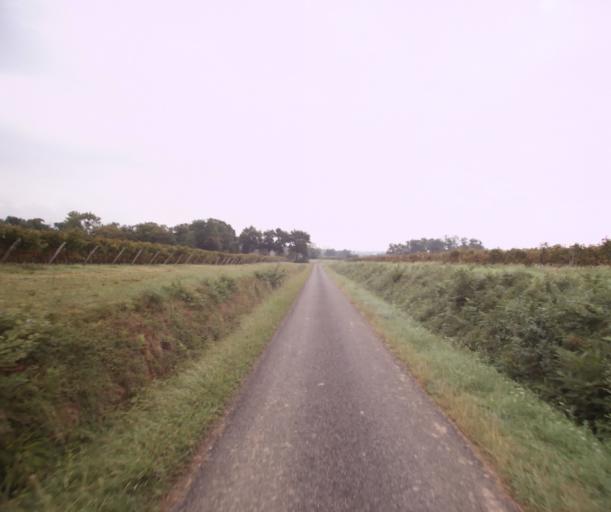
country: FR
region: Midi-Pyrenees
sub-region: Departement du Gers
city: Cazaubon
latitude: 43.9181
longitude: -0.1283
